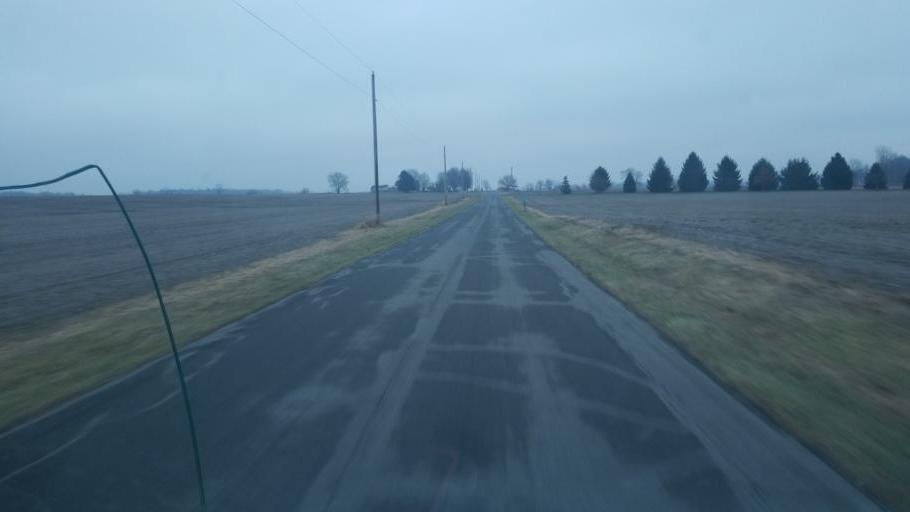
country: US
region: Ohio
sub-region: Seneca County
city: Tiffin
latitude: 40.9937
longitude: -83.1612
